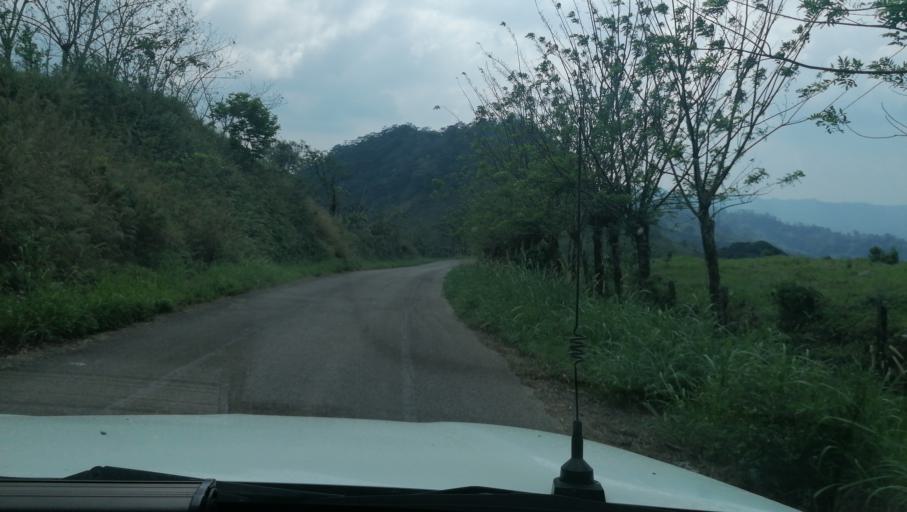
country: MX
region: Chiapas
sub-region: Francisco Leon
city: San Miguel la Sardina
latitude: 17.2379
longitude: -93.3189
